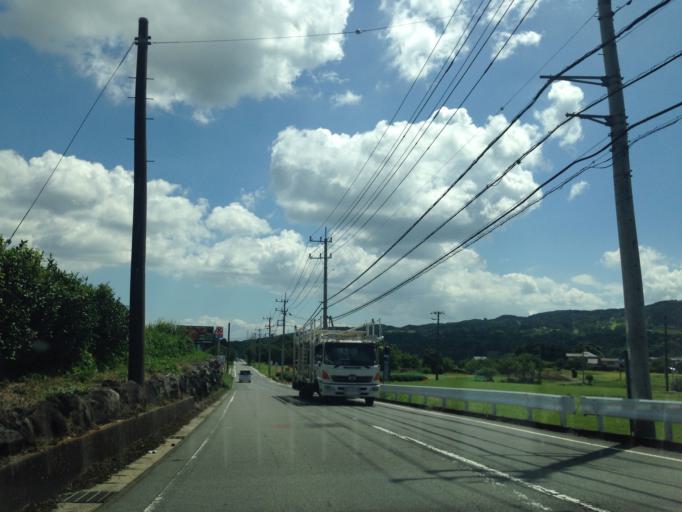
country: JP
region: Shizuoka
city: Gotemba
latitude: 35.2358
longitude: 138.8774
